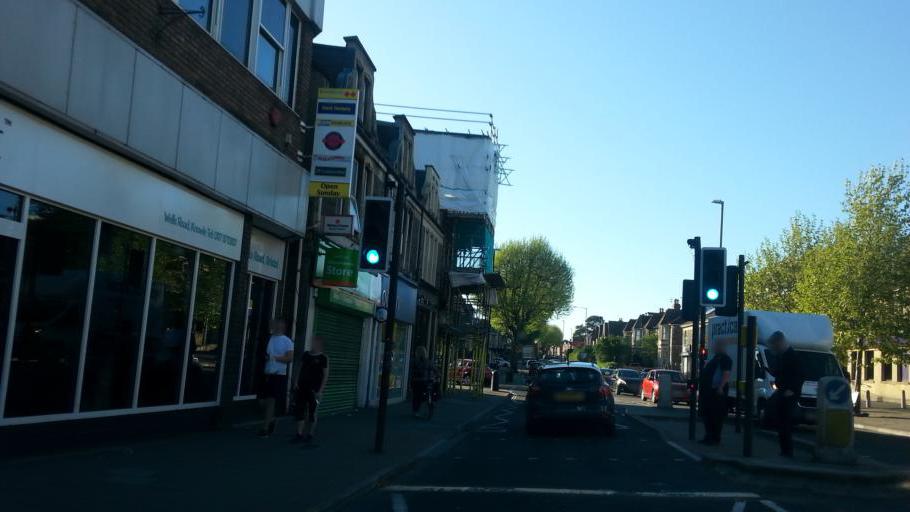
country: GB
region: England
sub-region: Bath and North East Somerset
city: Whitchurch
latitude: 51.4348
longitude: -2.5670
